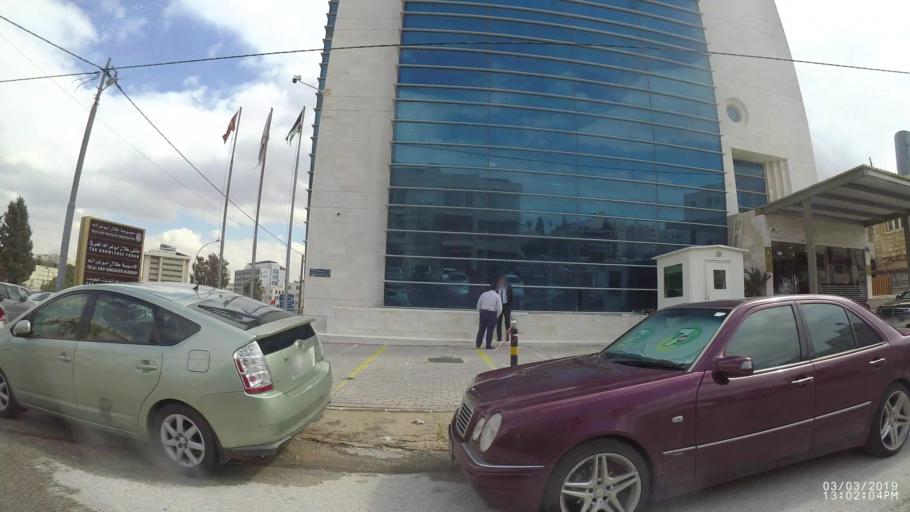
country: JO
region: Amman
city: Amman
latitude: 31.9697
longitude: 35.9045
